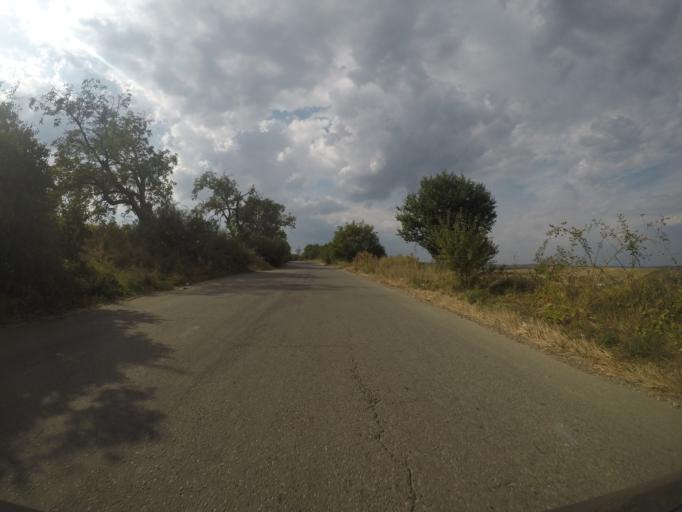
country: RO
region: Cluj
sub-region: Comuna Sandulesti
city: Copaceni
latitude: 46.5841
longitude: 23.7535
